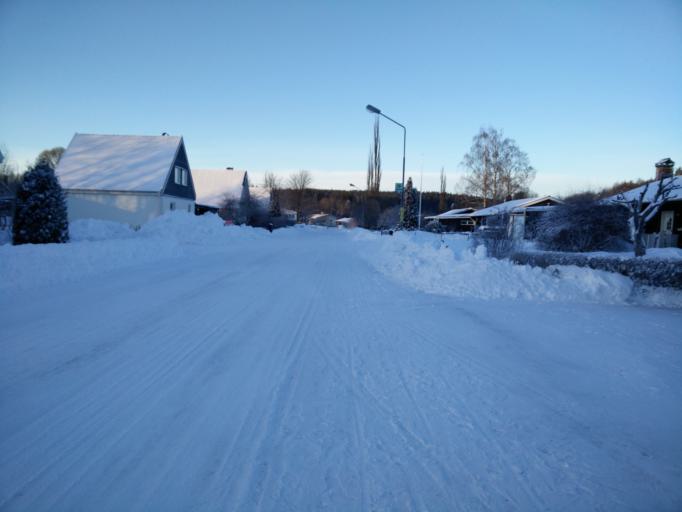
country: SE
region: Vaesternorrland
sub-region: Sundsvalls Kommun
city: Nolby
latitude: 62.2940
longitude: 17.3629
